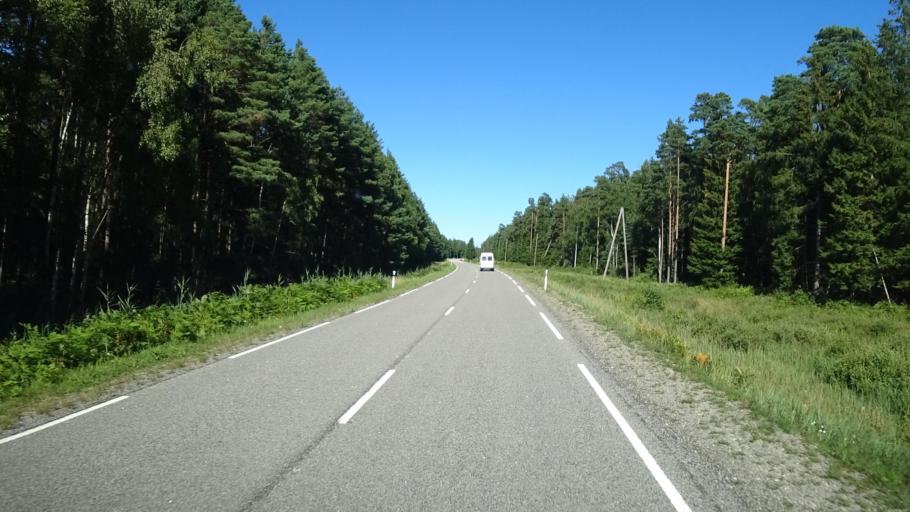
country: LV
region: Dundaga
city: Dundaga
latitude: 57.7212
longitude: 22.4803
